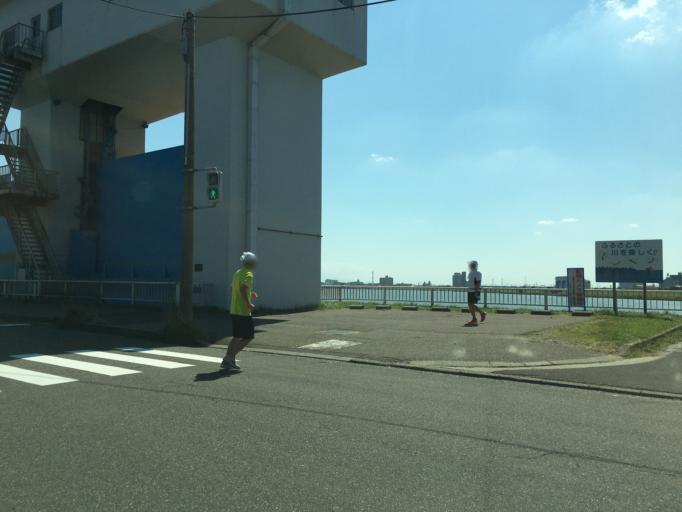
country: JP
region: Niigata
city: Niigata-shi
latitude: 37.8972
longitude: 139.0122
